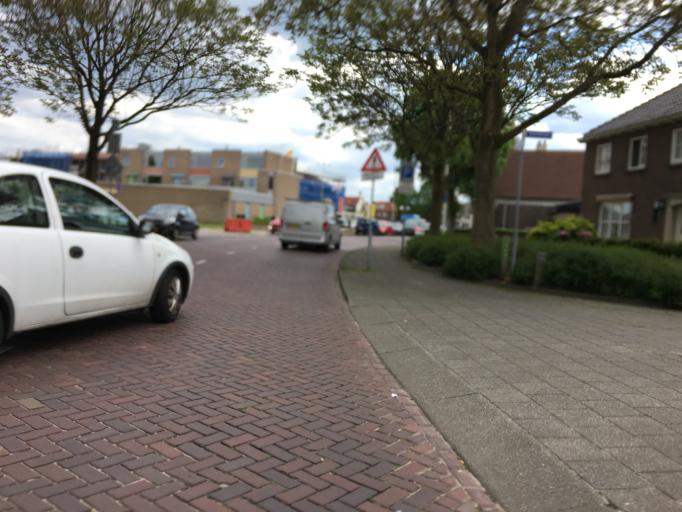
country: NL
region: Gelderland
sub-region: Gemeente Maasdriel
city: Hedel
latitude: 51.6967
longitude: 5.2188
